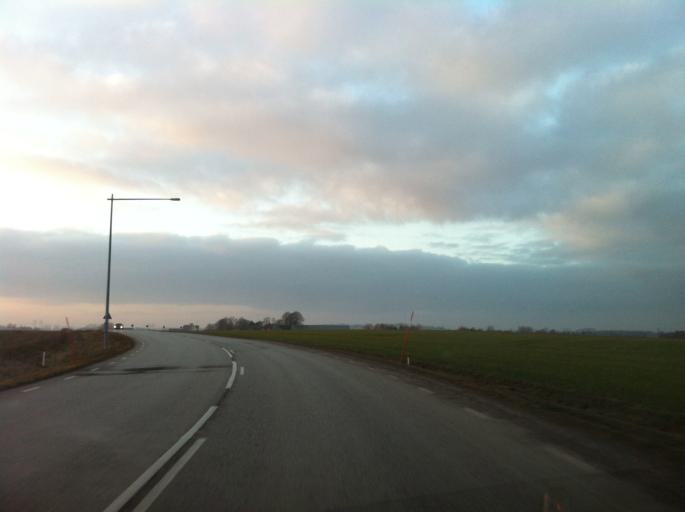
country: SE
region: Skane
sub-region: Kavlinge Kommun
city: Kaevlinge
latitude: 55.8003
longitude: 13.0966
